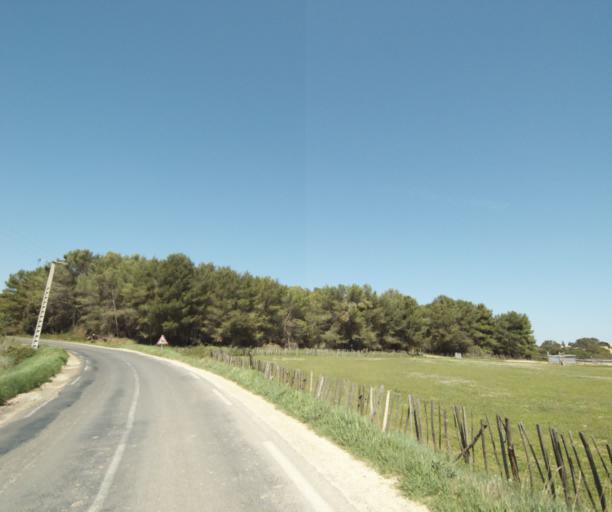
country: FR
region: Languedoc-Roussillon
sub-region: Departement de l'Herault
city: Saint-Genies-des-Mourgues
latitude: 43.6878
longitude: 4.0190
